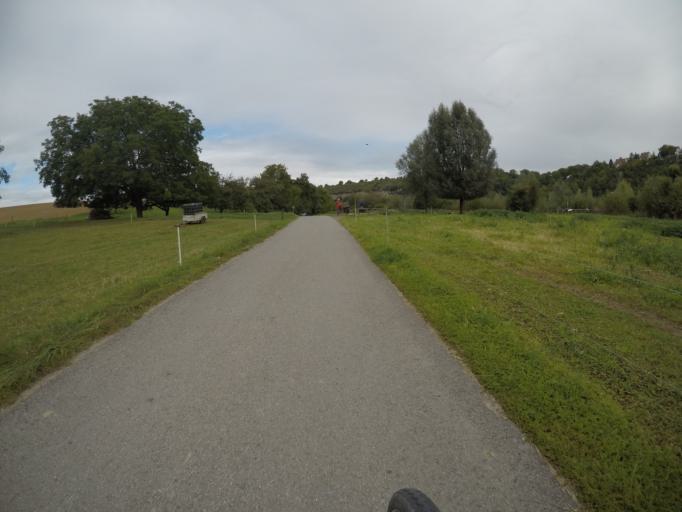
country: DE
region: Baden-Wuerttemberg
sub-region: Regierungsbezirk Stuttgart
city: Marbach am Neckar
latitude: 48.9072
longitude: 9.2565
